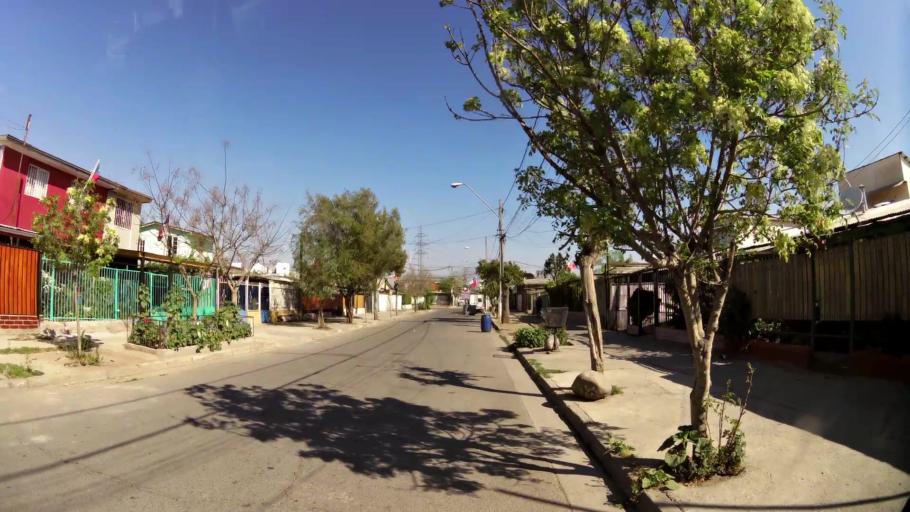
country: CL
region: Santiago Metropolitan
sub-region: Provincia de Santiago
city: La Pintana
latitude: -33.6191
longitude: -70.6195
